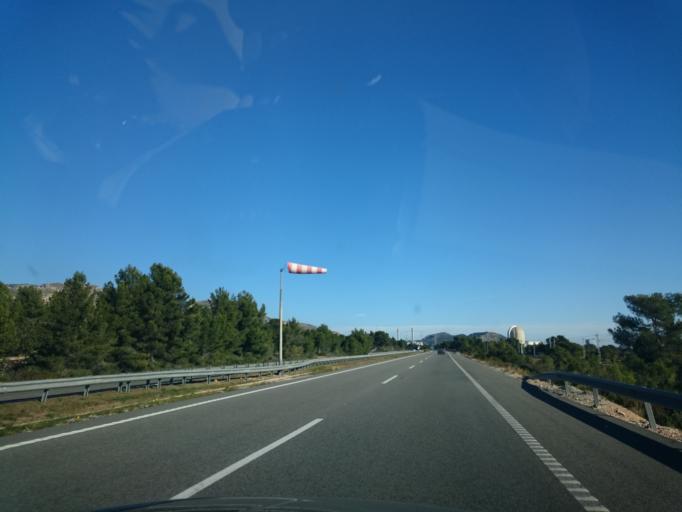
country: ES
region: Catalonia
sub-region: Provincia de Tarragona
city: l'Ametlla de Mar
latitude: 40.9421
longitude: 0.8532
